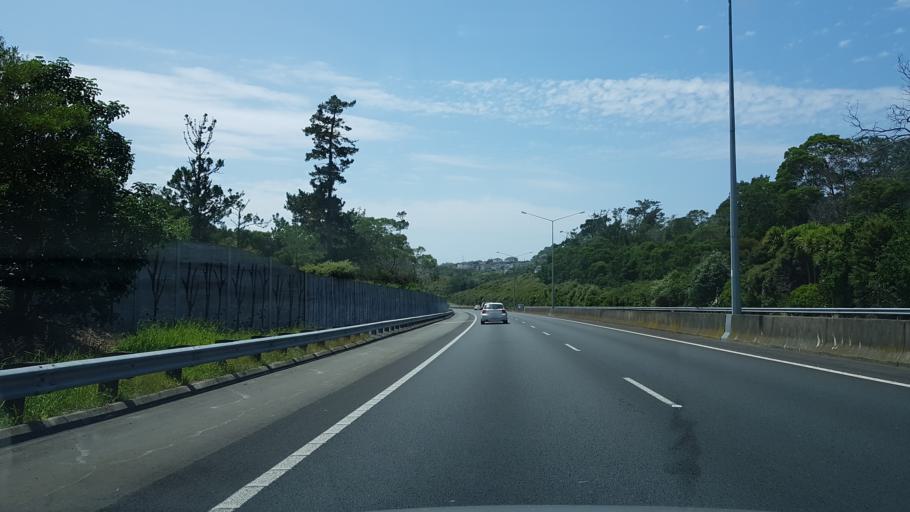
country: NZ
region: Auckland
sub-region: Auckland
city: North Shore
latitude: -36.7771
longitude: 174.6824
